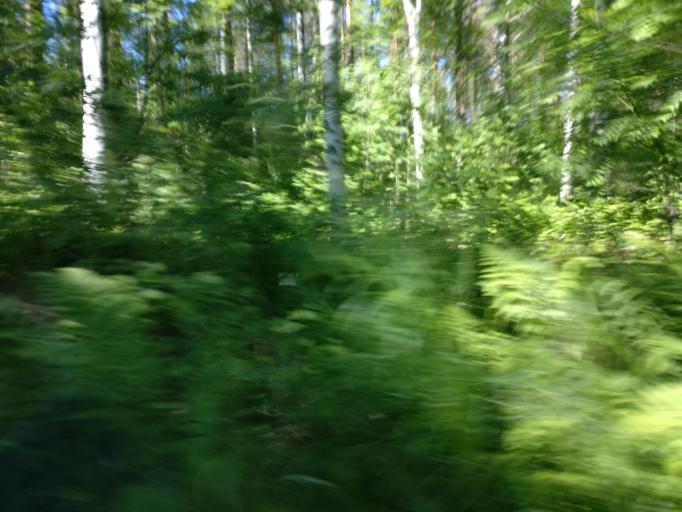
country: FI
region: Northern Savo
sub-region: Varkaus
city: Kangaslampi
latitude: 62.1779
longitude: 28.2337
